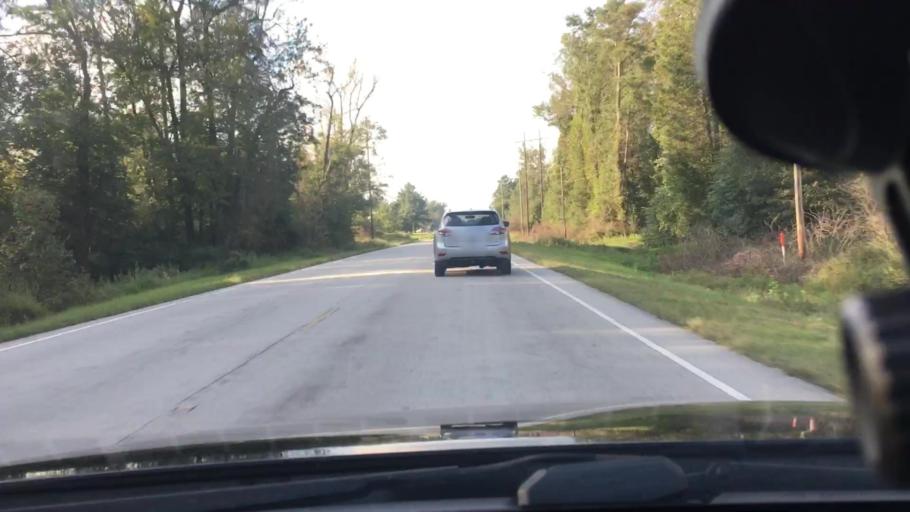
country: US
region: North Carolina
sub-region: Pitt County
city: Windsor
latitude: 35.4906
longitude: -77.3062
